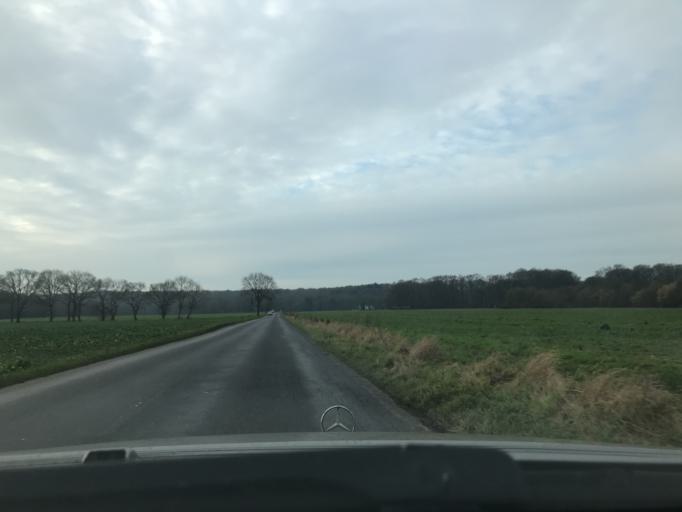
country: DE
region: North Rhine-Westphalia
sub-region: Regierungsbezirk Dusseldorf
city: Krefeld
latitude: 51.3992
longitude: 6.5451
